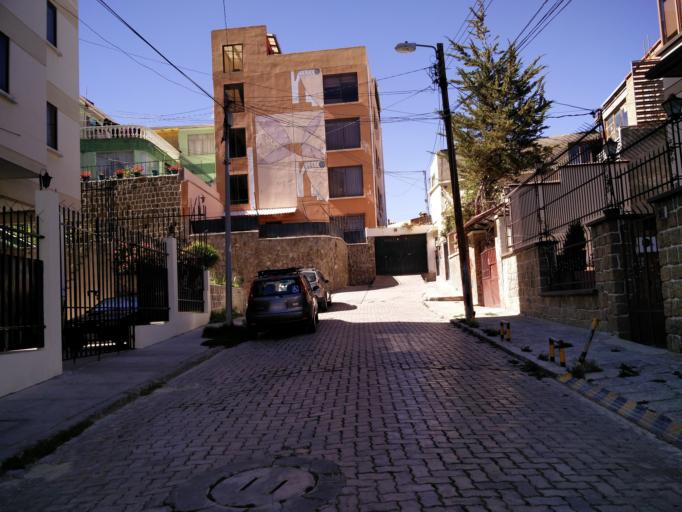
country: BO
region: La Paz
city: La Paz
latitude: -16.5105
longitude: -68.1314
